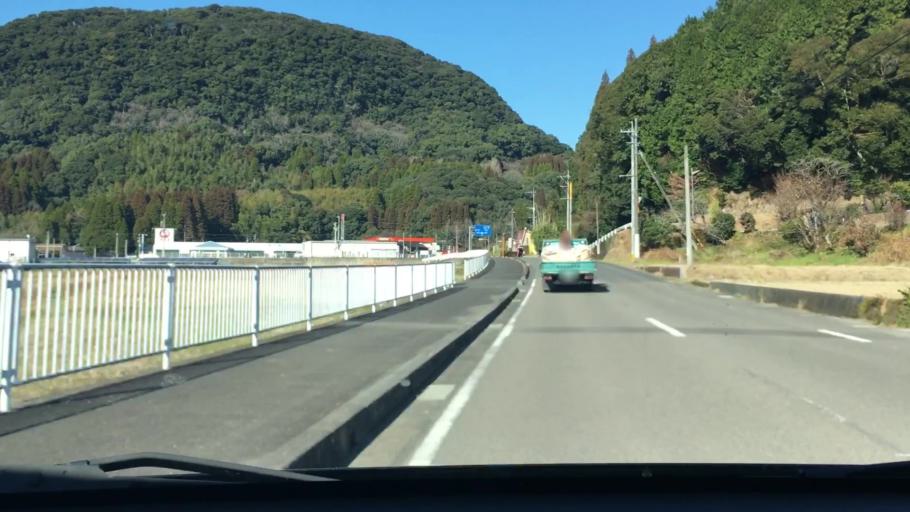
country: JP
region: Kagoshima
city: Satsumasendai
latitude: 31.7953
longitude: 130.4104
